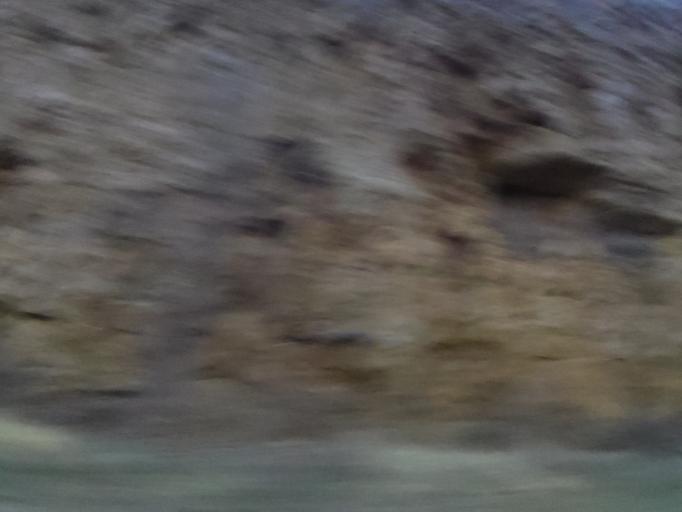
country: US
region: Wisconsin
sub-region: Saint Croix County
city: Hudson
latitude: 44.9545
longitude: -92.7161
